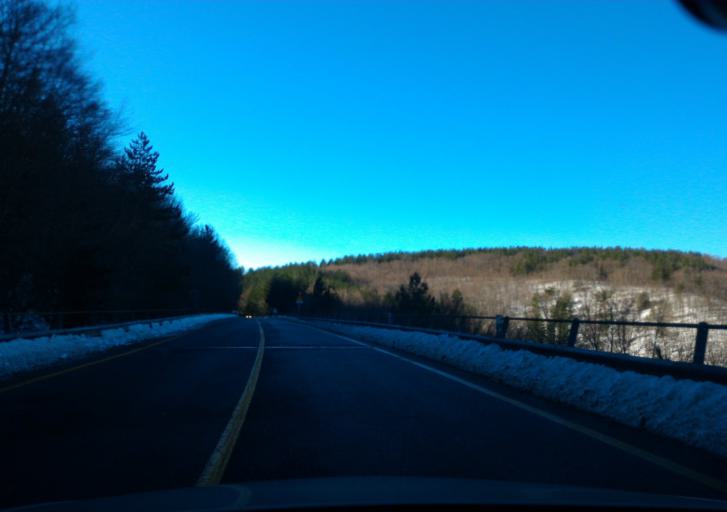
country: IT
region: Calabria
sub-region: Provincia di Cosenza
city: Celico
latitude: 39.3535
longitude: 16.3966
